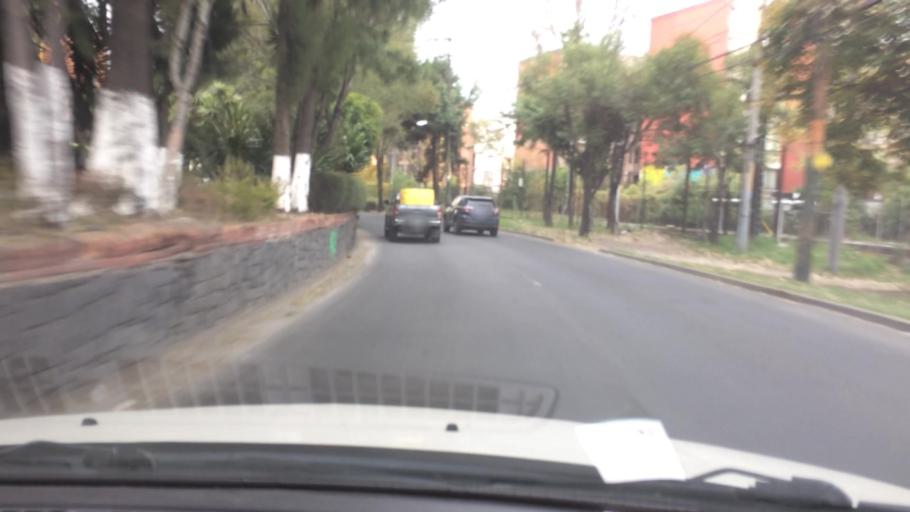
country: MX
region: Mexico City
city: Xochimilco
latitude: 19.2780
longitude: -99.1324
